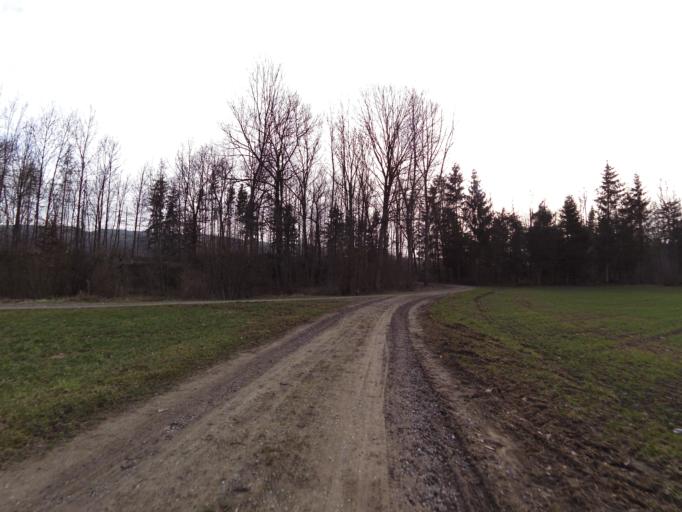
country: CH
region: Thurgau
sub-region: Frauenfeld District
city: Mullheim
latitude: 47.5891
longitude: 8.9812
